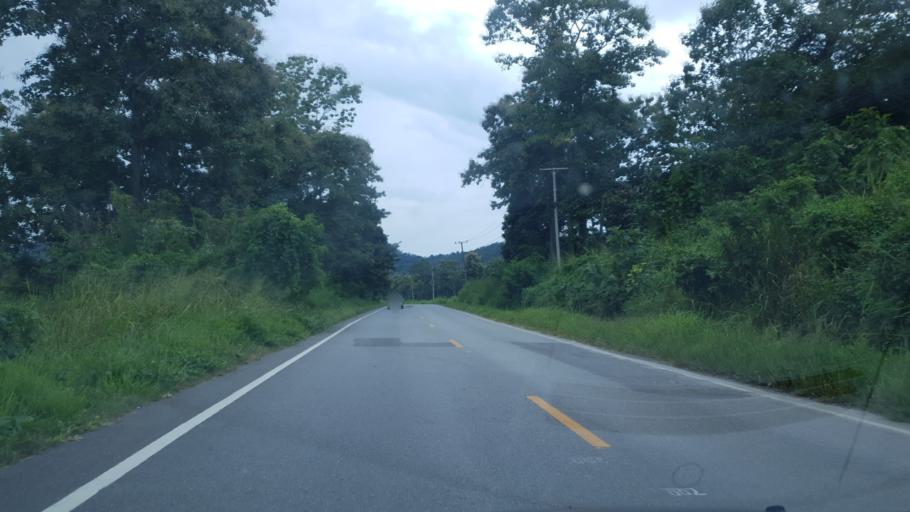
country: TH
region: Mae Hong Son
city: Khun Yuam
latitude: 18.7327
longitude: 97.9188
